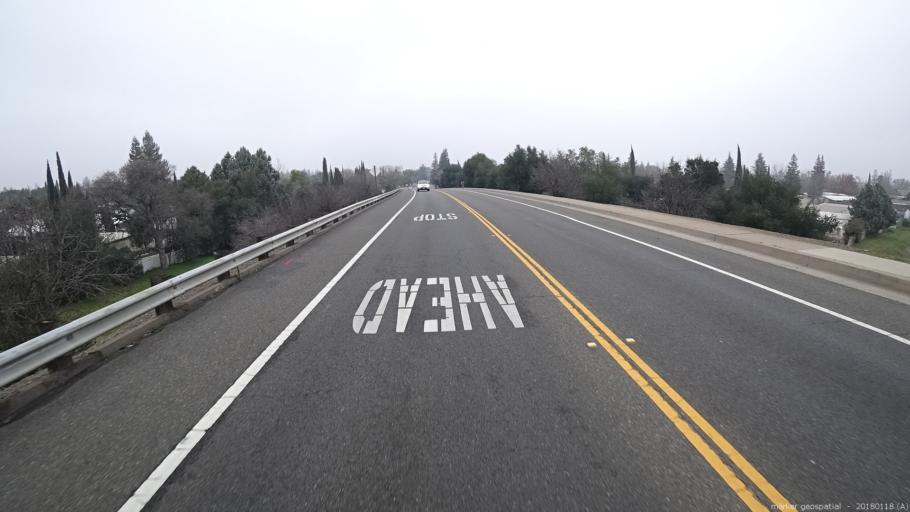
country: US
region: California
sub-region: Sacramento County
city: Rancho Cordova
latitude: 38.5749
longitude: -121.3179
